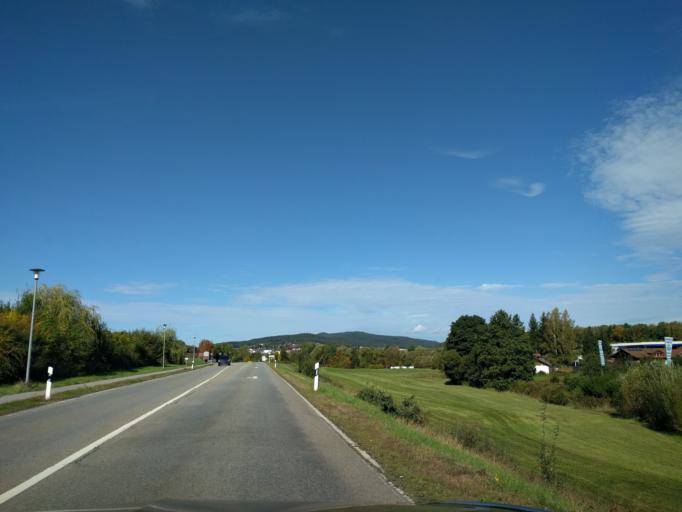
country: DE
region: Bavaria
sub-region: Upper Palatinate
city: Kotzting
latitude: 49.1677
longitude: 12.8709
